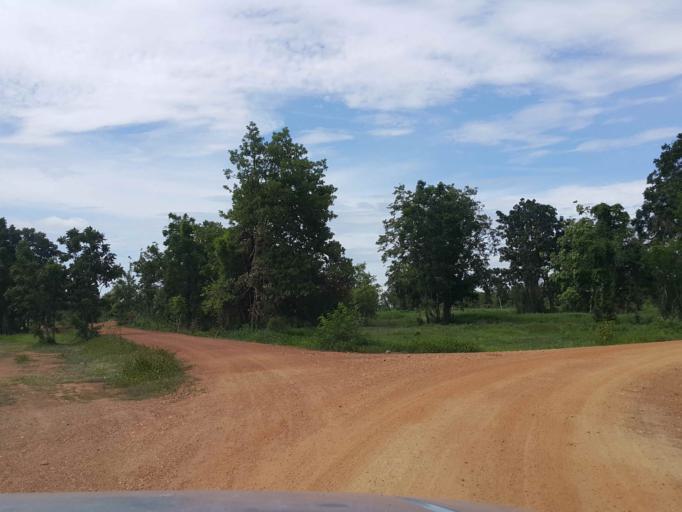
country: TH
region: Sukhothai
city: Ban Dan Lan Hoi
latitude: 17.1022
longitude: 99.4681
